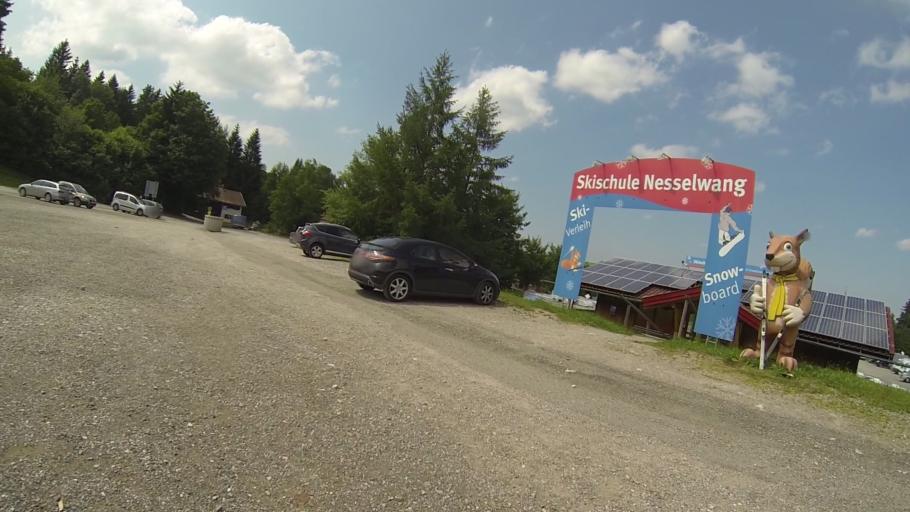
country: DE
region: Bavaria
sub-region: Swabia
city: Nesselwang
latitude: 47.6191
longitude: 10.4980
